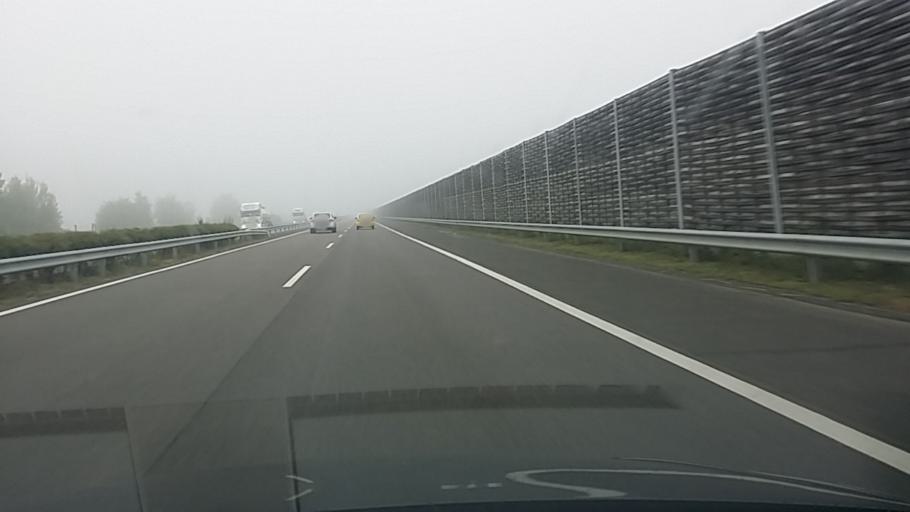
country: HU
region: Csongrad
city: Domaszek
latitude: 46.2758
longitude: 20.0404
